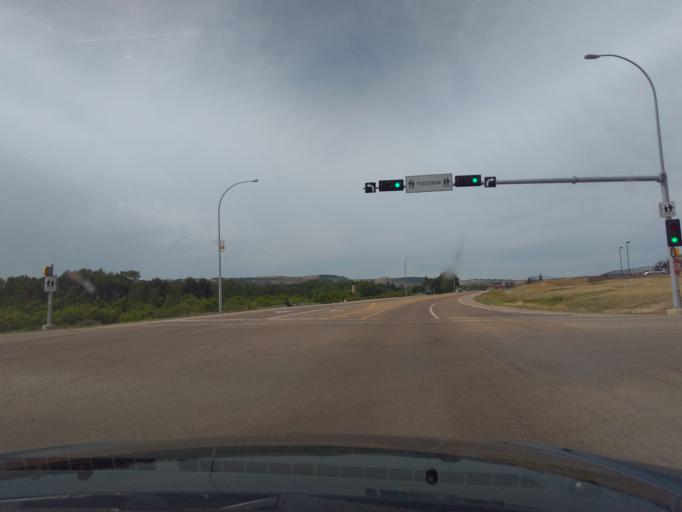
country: CA
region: Alberta
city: Three Hills
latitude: 51.4707
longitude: -112.7301
